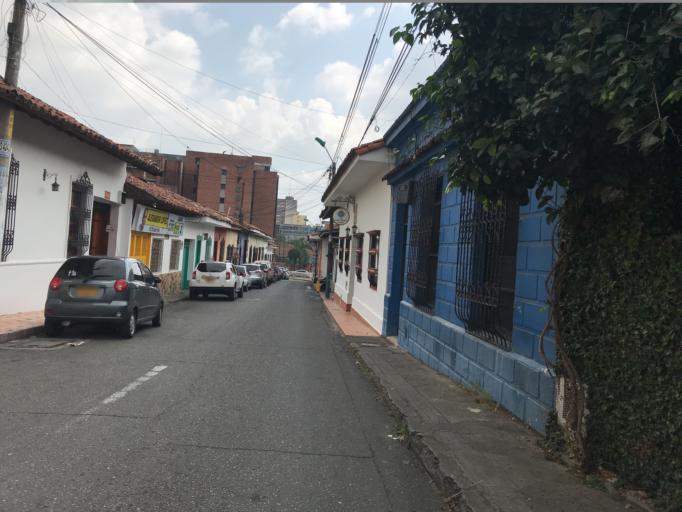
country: CO
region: Valle del Cauca
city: Cali
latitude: 3.4470
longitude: -76.5379
